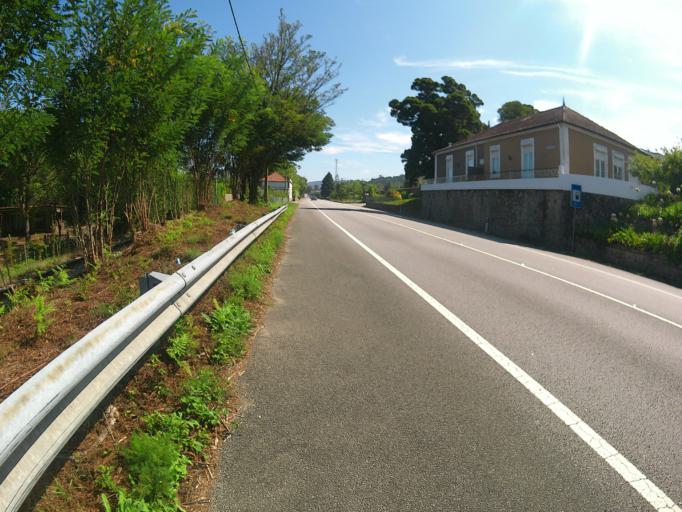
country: ES
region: Galicia
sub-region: Provincia de Pontevedra
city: O Rosal
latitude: 41.9065
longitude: -8.7968
